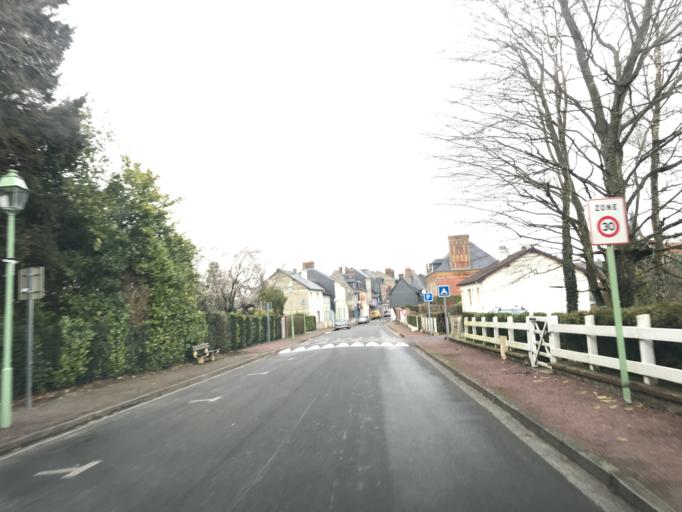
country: FR
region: Lower Normandy
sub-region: Departement du Calvados
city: Touques
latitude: 49.2766
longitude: 0.1089
